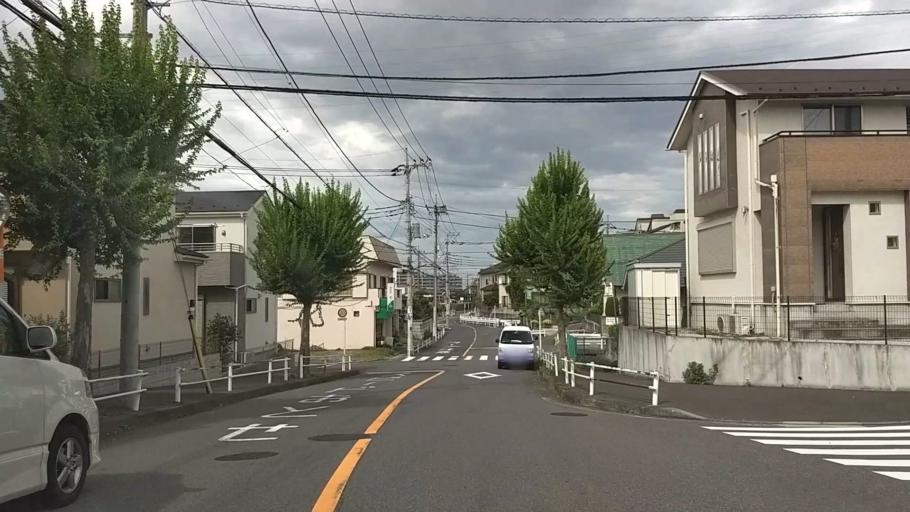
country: JP
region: Tokyo
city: Hachioji
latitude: 35.6411
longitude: 139.3460
